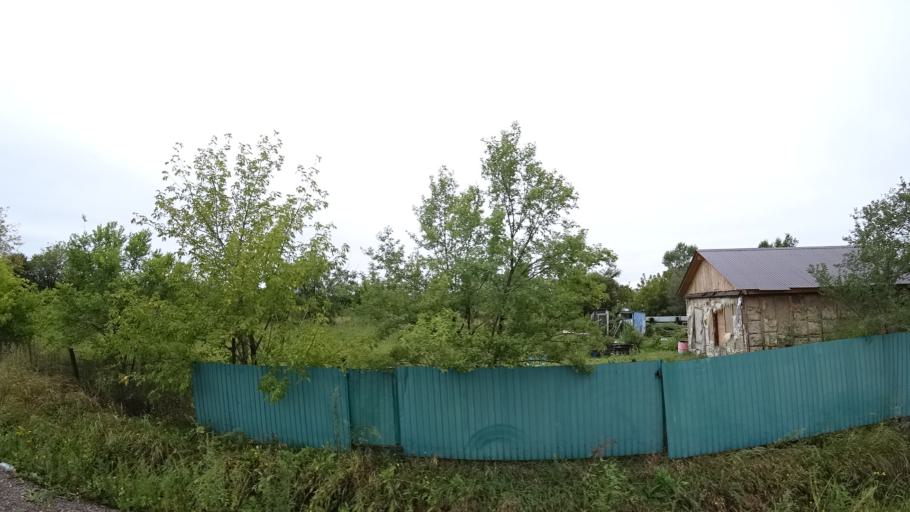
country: RU
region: Primorskiy
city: Monastyrishche
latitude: 44.1987
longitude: 132.4968
